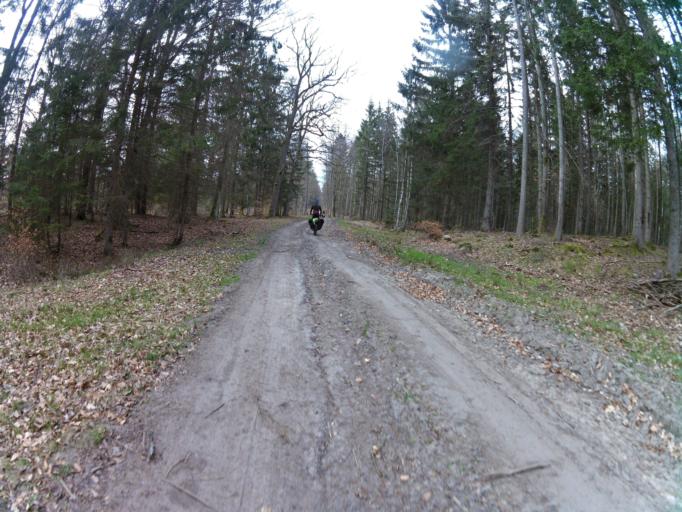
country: PL
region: West Pomeranian Voivodeship
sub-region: Powiat szczecinecki
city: Bialy Bor
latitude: 53.8910
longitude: 16.7183
